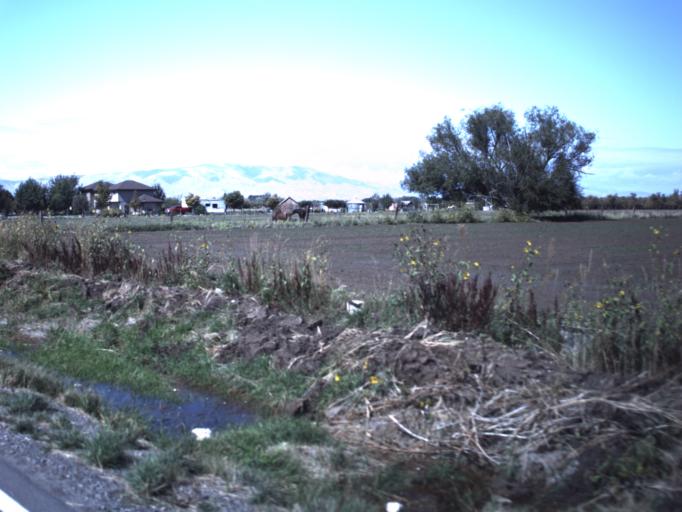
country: US
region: Utah
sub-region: Utah County
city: Benjamin
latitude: 40.1584
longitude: -111.7082
